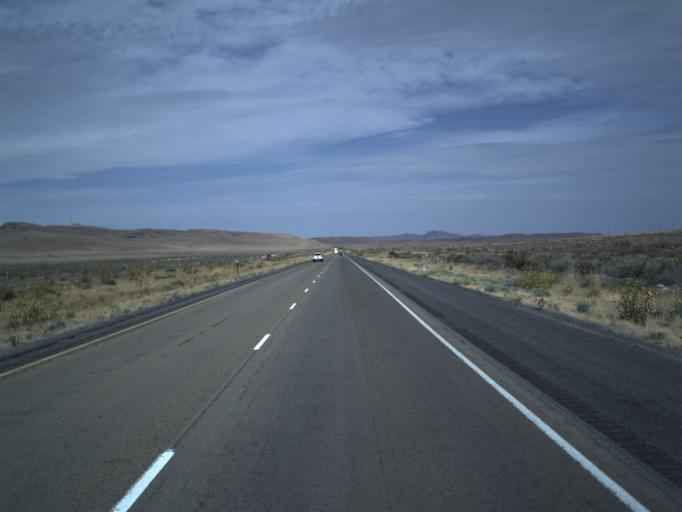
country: US
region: Utah
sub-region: Tooele County
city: Grantsville
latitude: 40.7788
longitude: -112.8102
